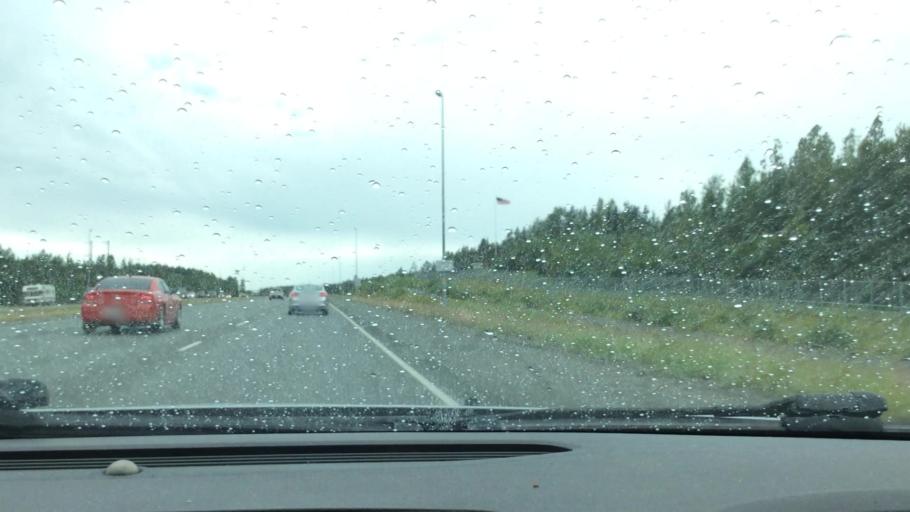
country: US
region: Alaska
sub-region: Anchorage Municipality
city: Elmendorf Air Force Base
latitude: 61.2506
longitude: -149.6670
